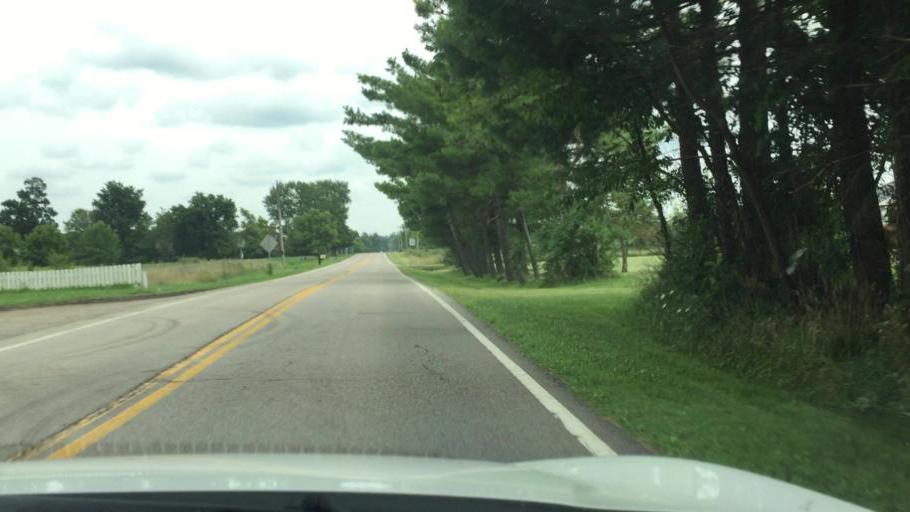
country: US
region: Ohio
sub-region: Champaign County
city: North Lewisburg
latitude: 40.2392
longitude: -83.4738
